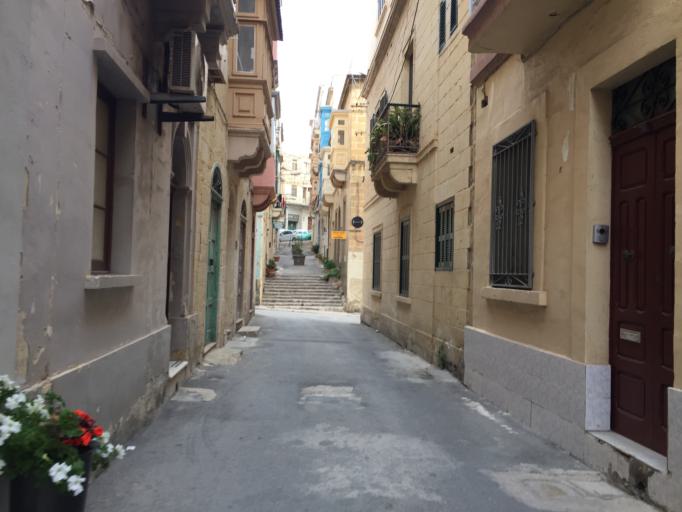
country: MT
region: L-Isla
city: Senglea
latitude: 35.8820
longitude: 14.5188
